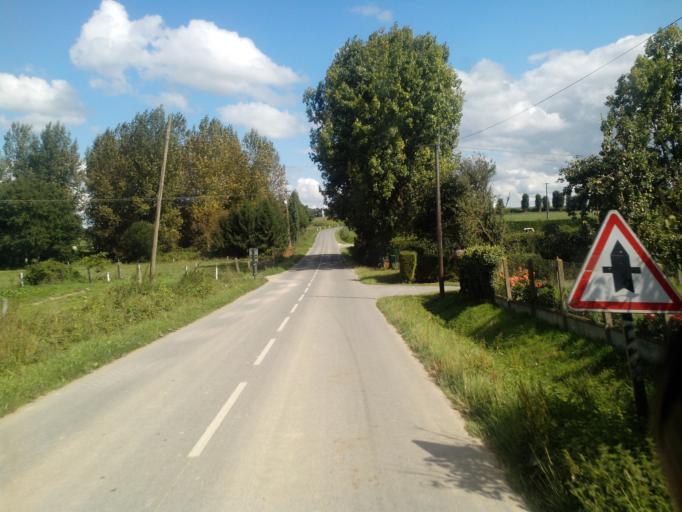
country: FR
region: Brittany
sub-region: Departement d'Ille-et-Vilaine
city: Gael
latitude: 48.1308
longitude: -2.2034
